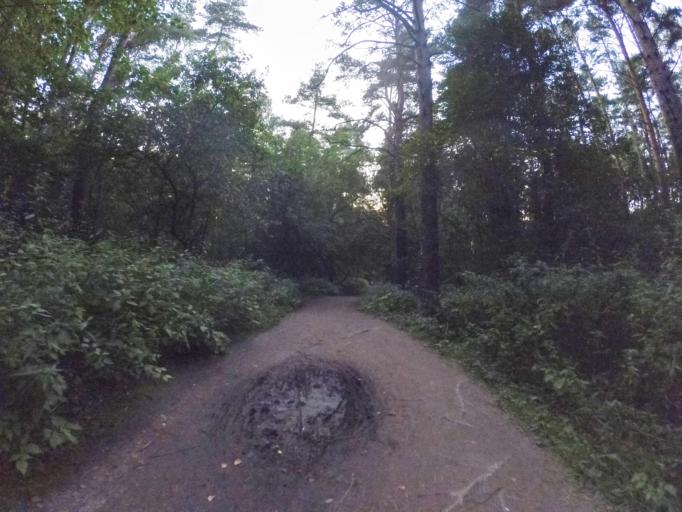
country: RU
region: Moskovskaya
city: Kotel'niki
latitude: 55.6664
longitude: 37.8444
